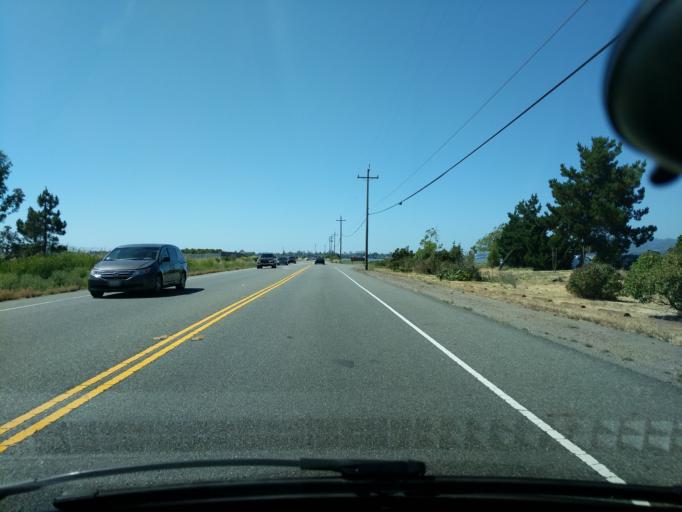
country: US
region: California
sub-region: Alameda County
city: Alameda
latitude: 37.7412
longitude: -122.2168
